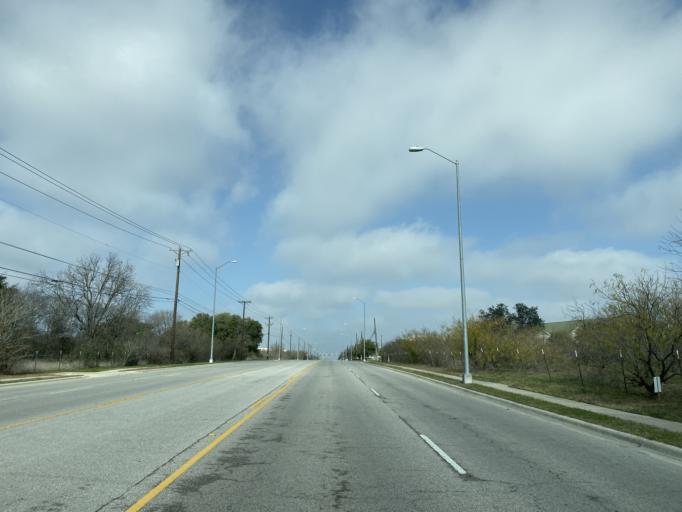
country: US
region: Texas
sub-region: Williamson County
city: Round Rock
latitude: 30.5318
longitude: -97.6951
